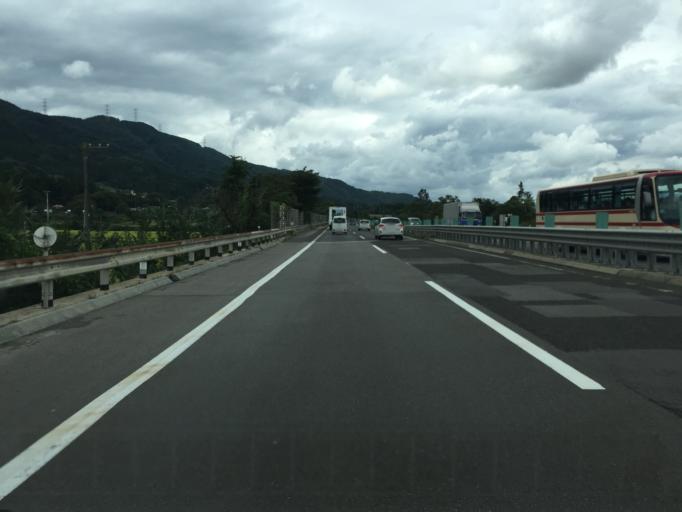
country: JP
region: Miyagi
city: Shiroishi
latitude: 37.9653
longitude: 140.6179
